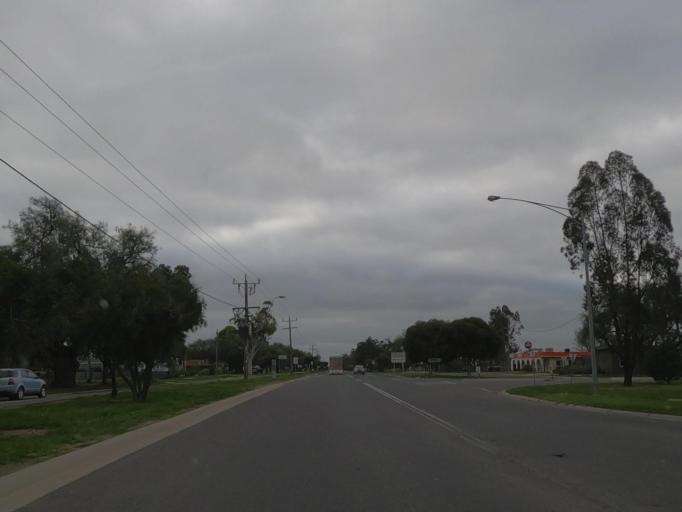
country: AU
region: Victoria
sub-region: Greater Bendigo
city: Long Gully
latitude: -36.4123
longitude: 143.9744
